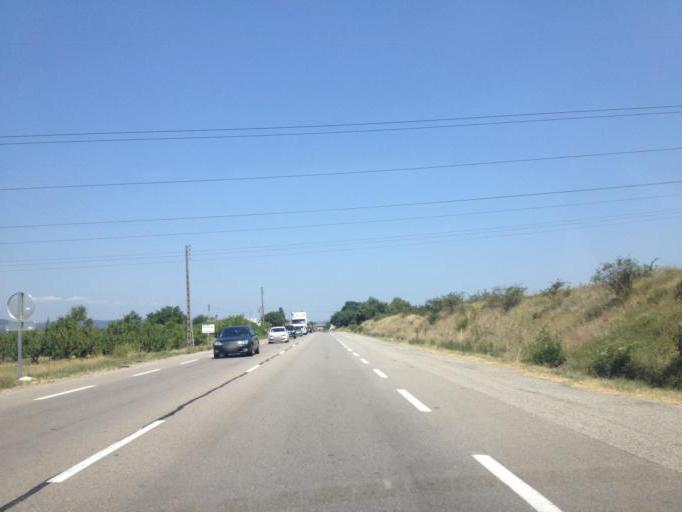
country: FR
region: Rhone-Alpes
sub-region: Departement de l'Ardeche
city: Cornas
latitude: 44.9828
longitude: 4.8812
